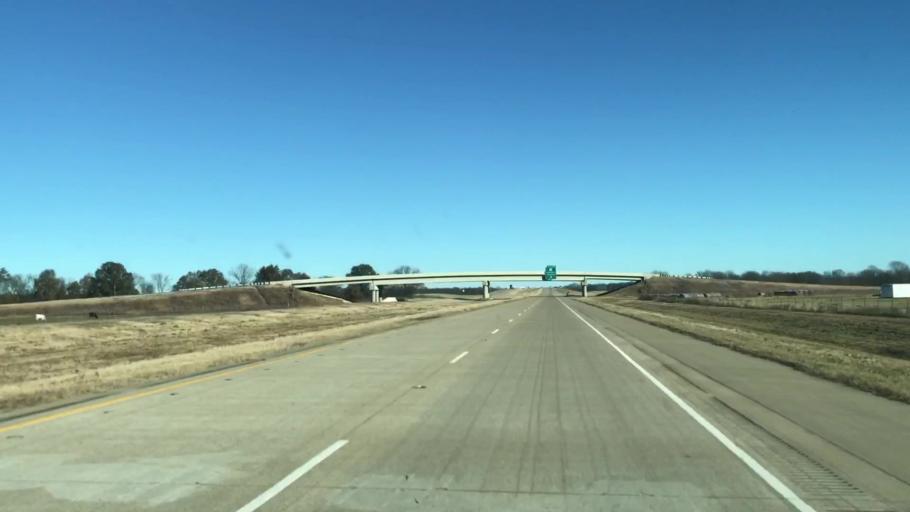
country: US
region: Louisiana
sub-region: Caddo Parish
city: Vivian
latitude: 32.8430
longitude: -93.8687
